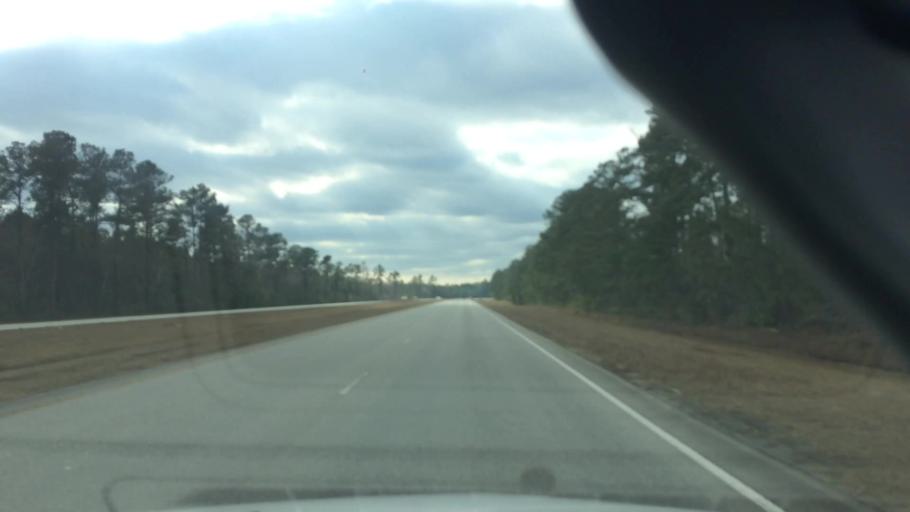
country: US
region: North Carolina
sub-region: Brunswick County
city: Bolivia
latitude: 34.0542
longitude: -78.2139
